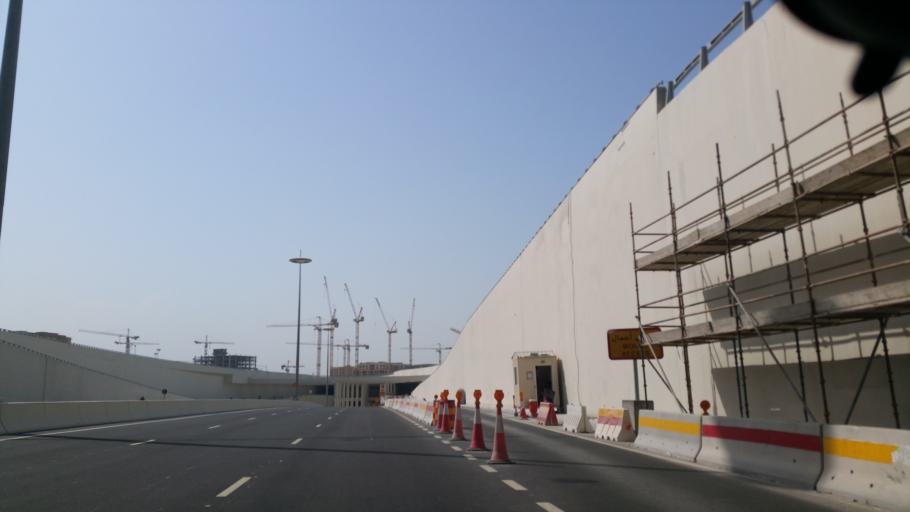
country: QA
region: Baladiyat Umm Salal
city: Umm Salal Muhammad
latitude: 25.4120
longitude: 51.5093
